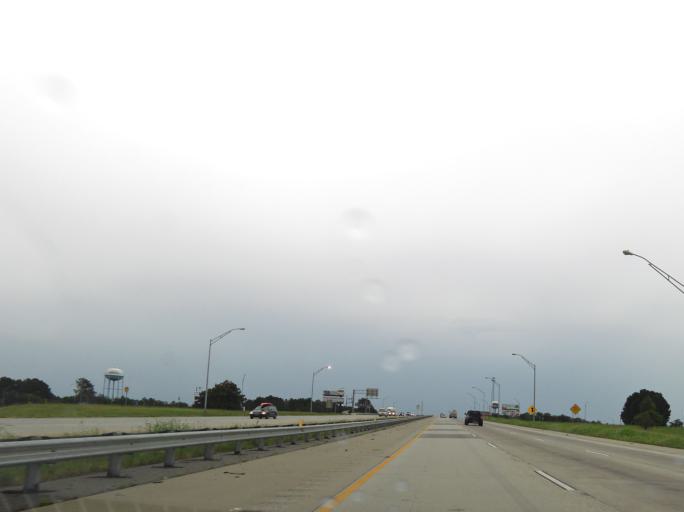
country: US
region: Georgia
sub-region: Dooly County
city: Unadilla
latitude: 32.2504
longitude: -83.7453
